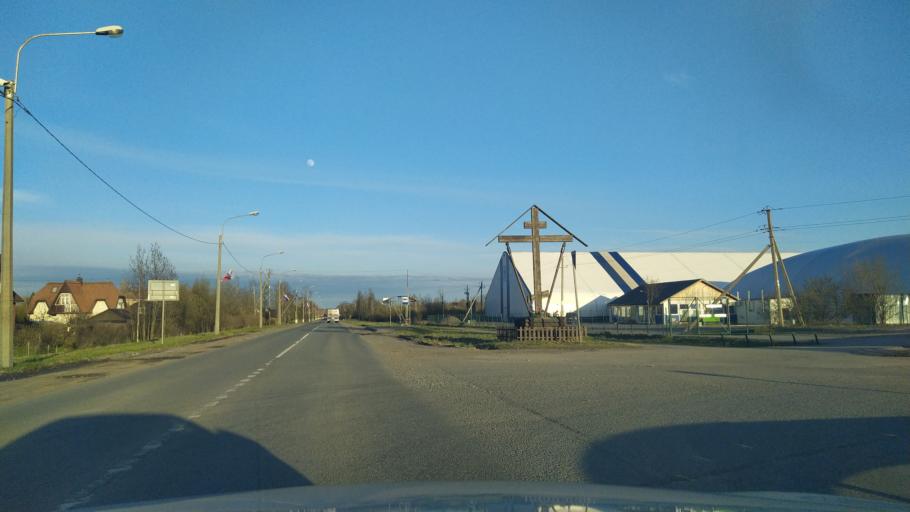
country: RU
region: St.-Petersburg
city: Aleksandrovskaya
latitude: 59.7386
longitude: 30.3249
